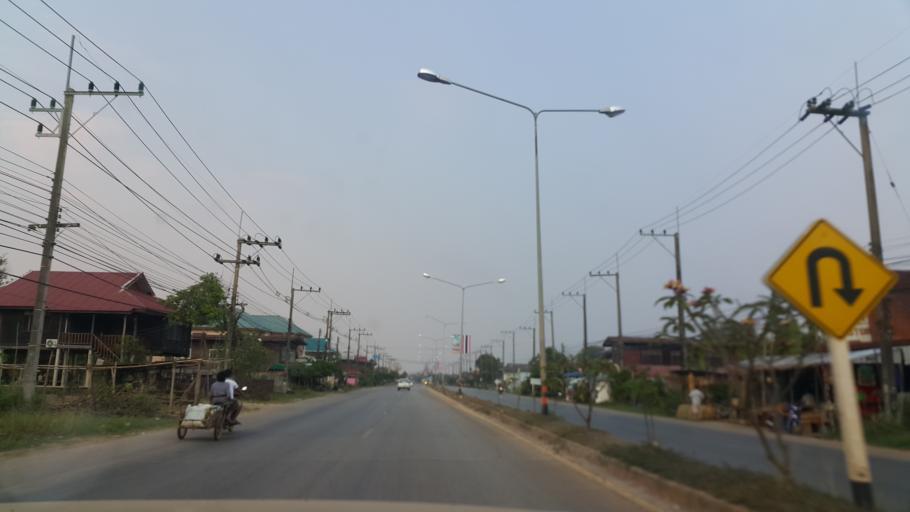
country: TH
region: Nakhon Phanom
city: That Phanom
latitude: 16.9730
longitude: 104.7272
